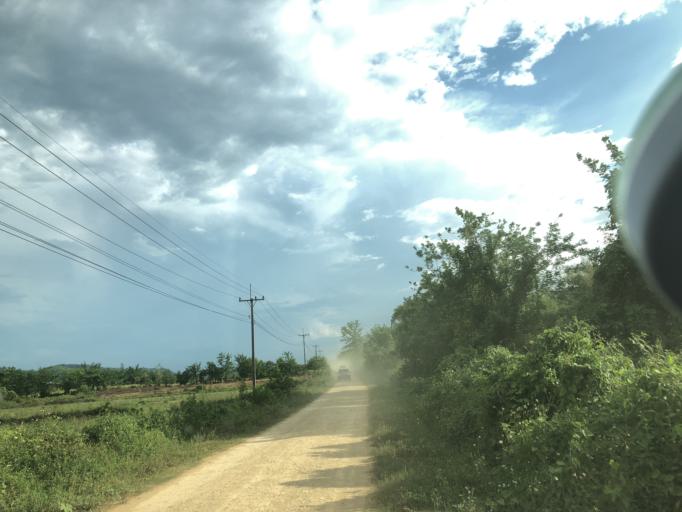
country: LA
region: Xiagnabouli
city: Muang Kenthao
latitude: 17.9903
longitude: 101.4186
